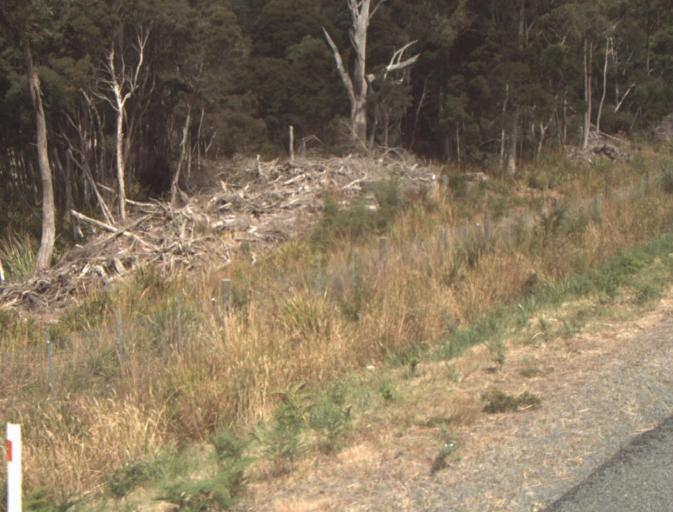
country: AU
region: Tasmania
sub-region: Launceston
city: Mayfield
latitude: -41.3039
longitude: 147.0488
